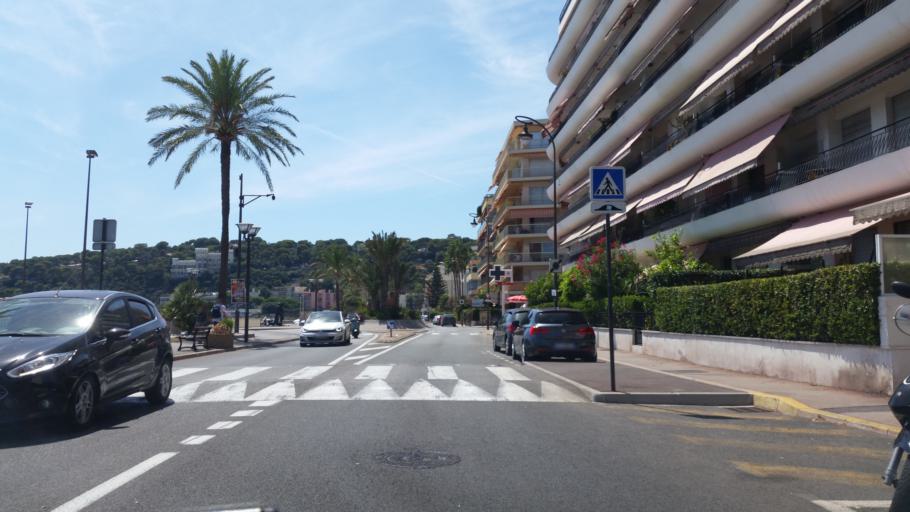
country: FR
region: Provence-Alpes-Cote d'Azur
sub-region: Departement des Alpes-Maritimes
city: Roquebrune-Cap-Martin
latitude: 43.7609
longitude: 7.4838
